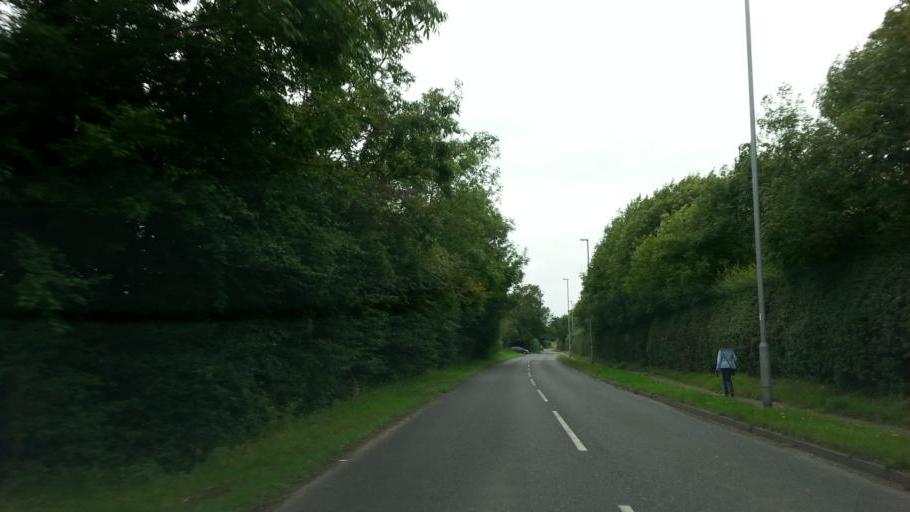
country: GB
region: England
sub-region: Nottinghamshire
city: Southwell
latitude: 53.0792
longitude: -0.9667
